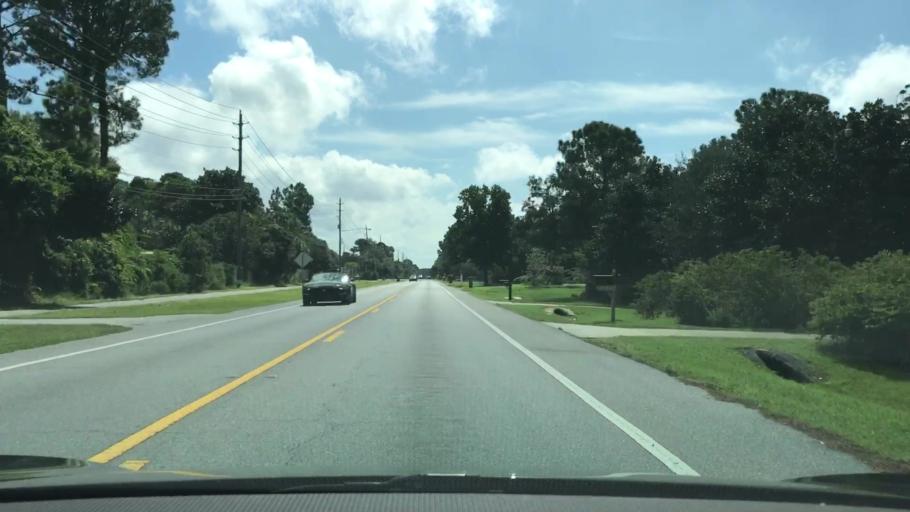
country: US
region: Florida
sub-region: Bay County
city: Panama City Beach
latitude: 30.1697
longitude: -85.7854
